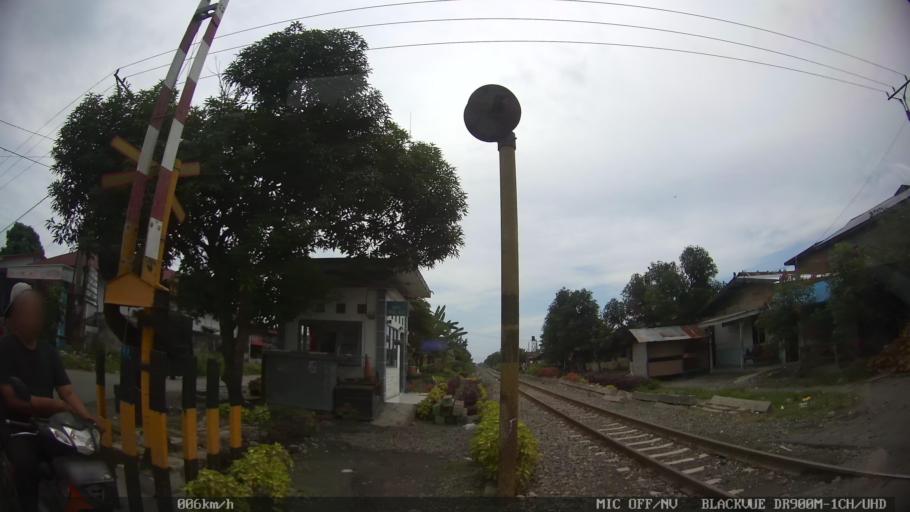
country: ID
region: North Sumatra
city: Sunggal
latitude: 3.6060
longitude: 98.5756
